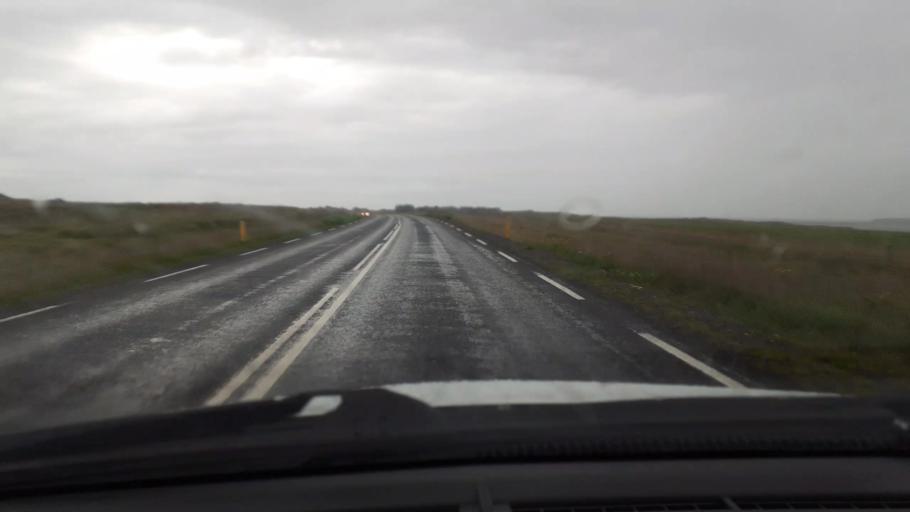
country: IS
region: West
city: Akranes
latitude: 64.3658
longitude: -21.9259
